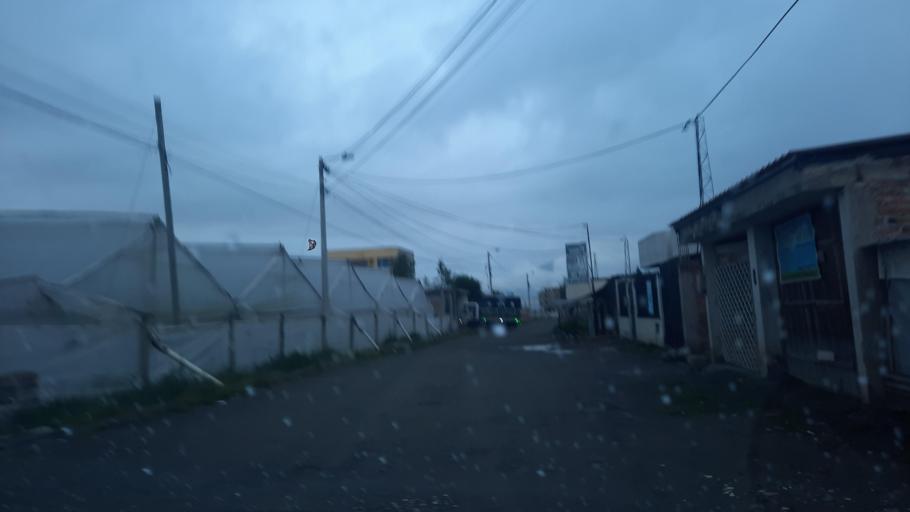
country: EC
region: Chimborazo
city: Riobamba
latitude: -1.6878
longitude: -78.6621
